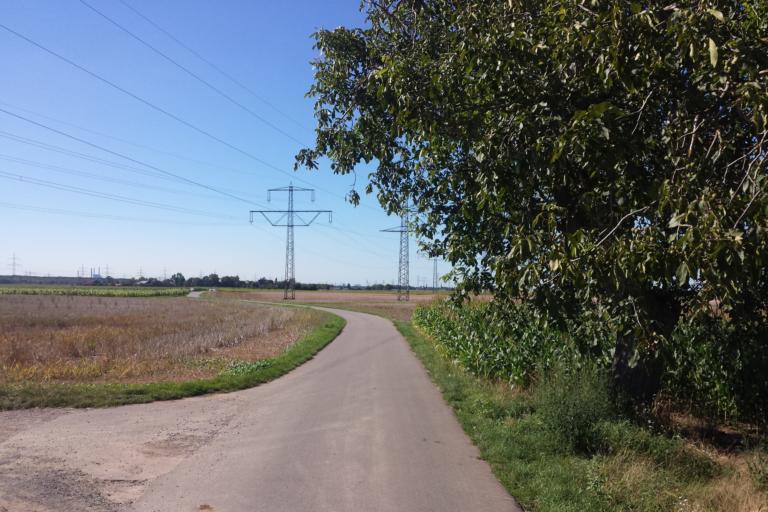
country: DE
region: Baden-Wuerttemberg
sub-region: Karlsruhe Region
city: Plankstadt
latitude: 49.4119
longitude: 8.6099
